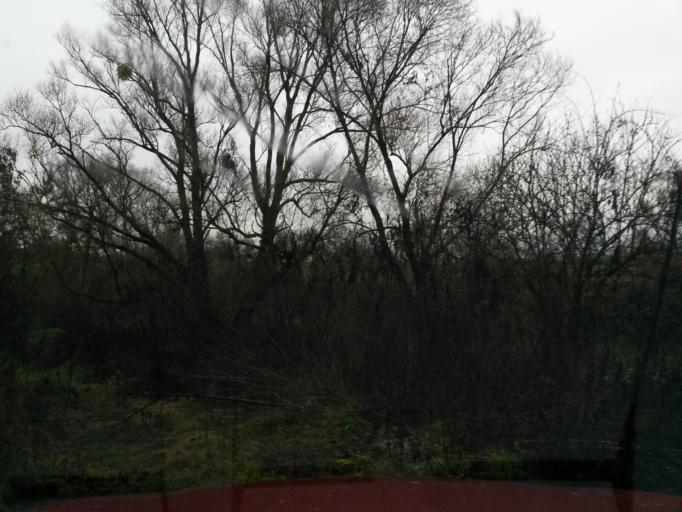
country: UA
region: Zakarpattia
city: Storozhnytsya
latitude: 48.6290
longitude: 22.1052
